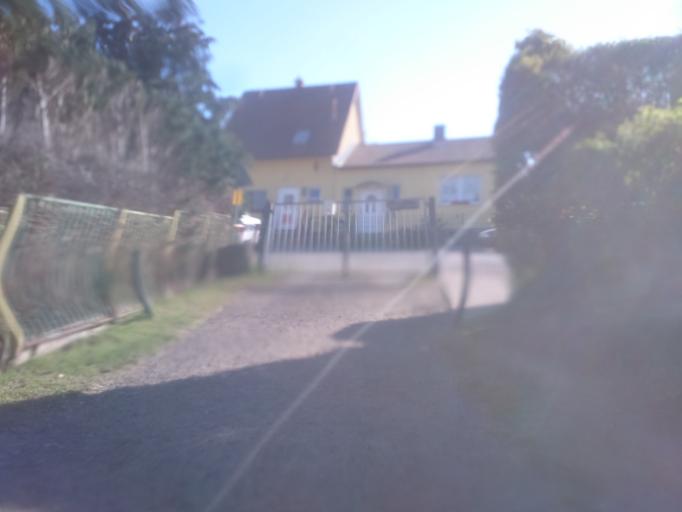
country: DE
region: Berlin
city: Alt-Hohenschoenhausen
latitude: 52.5539
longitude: 13.5056
